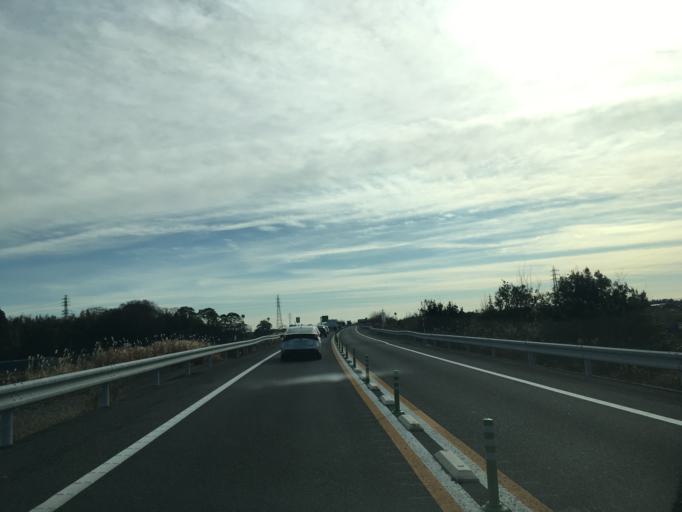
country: JP
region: Ibaraki
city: Naka
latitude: 36.0495
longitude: 140.1053
